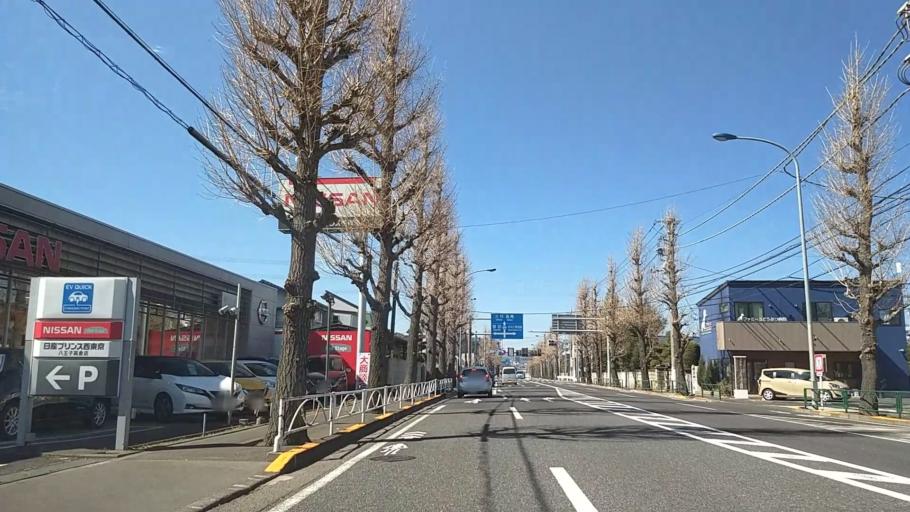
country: JP
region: Tokyo
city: Hino
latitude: 35.6678
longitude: 139.3684
